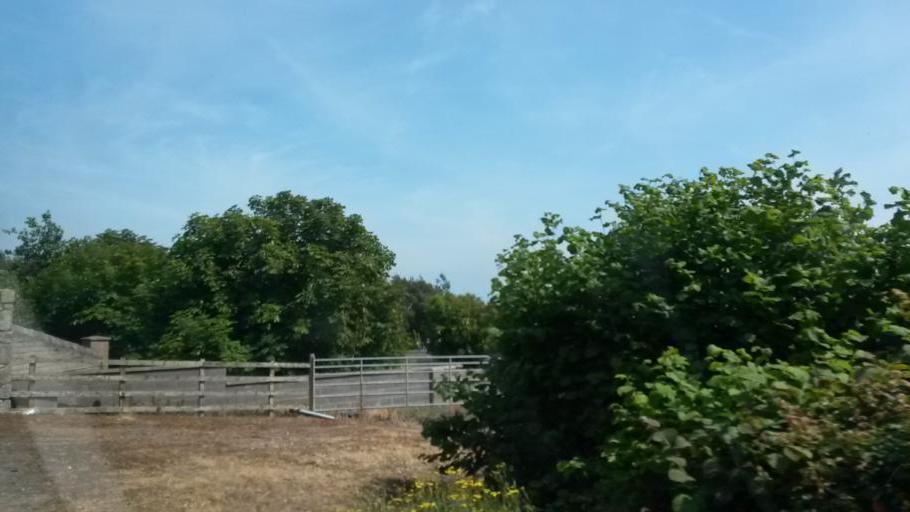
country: IE
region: Leinster
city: Lusk
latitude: 53.5075
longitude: -6.1704
